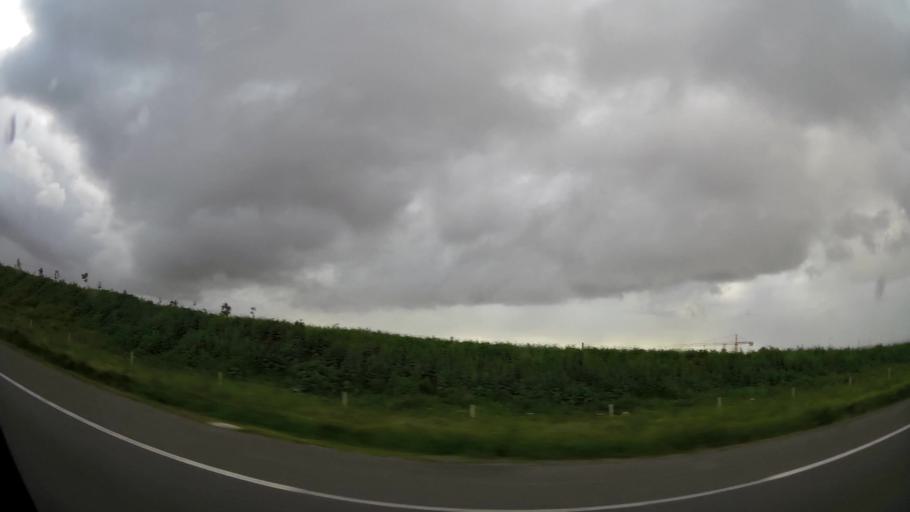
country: MA
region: Grand Casablanca
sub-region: Mohammedia
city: Mohammedia
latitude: 33.6281
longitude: -7.4270
